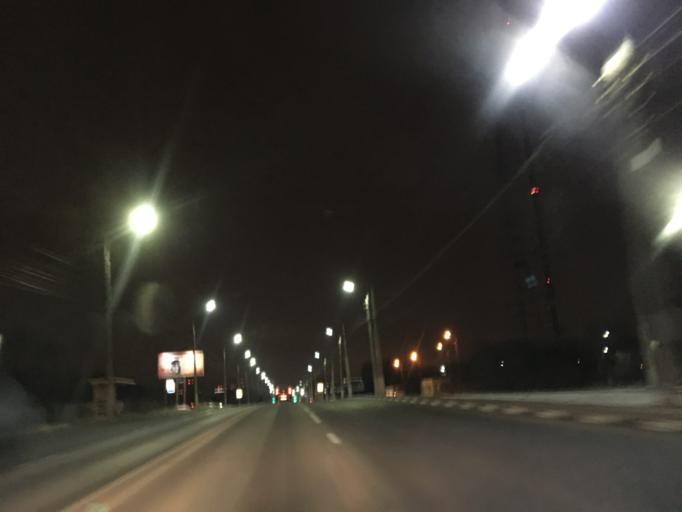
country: RU
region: Tula
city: Mendeleyevskiy
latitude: 54.1382
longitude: 37.5803
